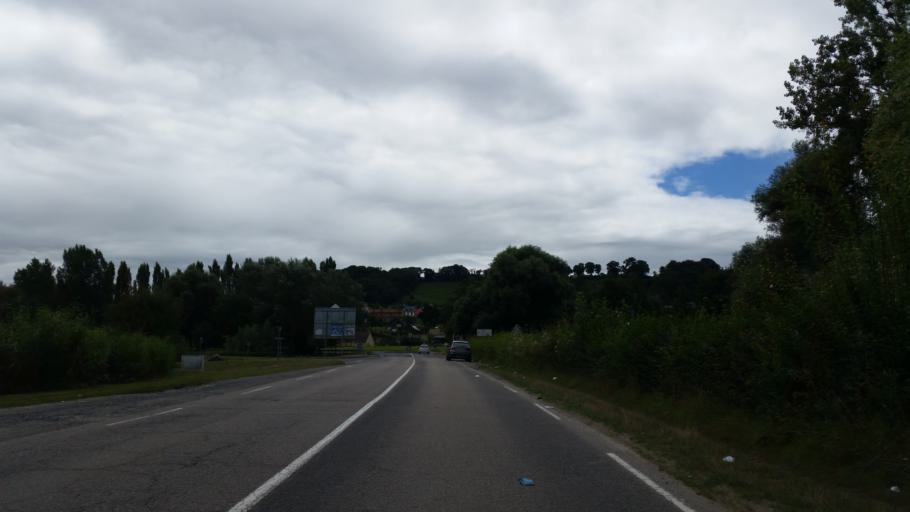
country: FR
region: Lower Normandy
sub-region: Departement du Calvados
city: La Riviere-Saint-Sauveur
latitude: 49.4132
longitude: 0.2590
